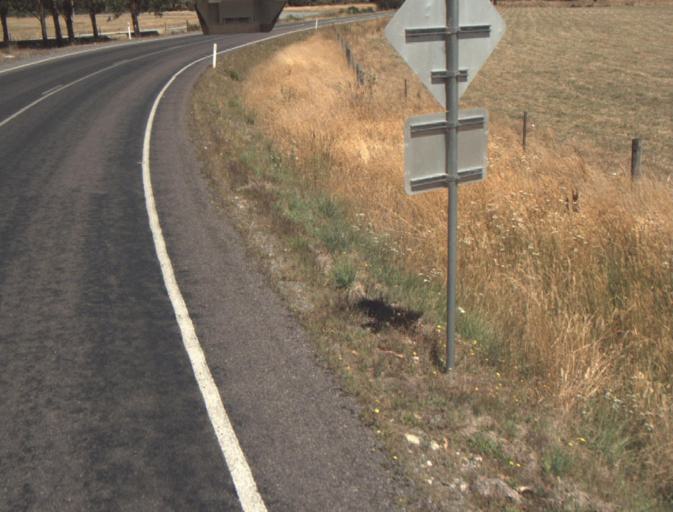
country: AU
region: Tasmania
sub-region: Launceston
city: Newstead
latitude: -41.3295
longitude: 147.3535
